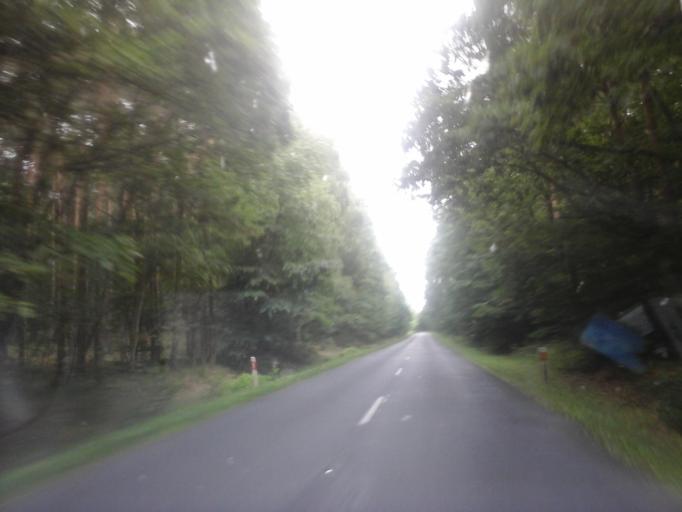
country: PL
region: West Pomeranian Voivodeship
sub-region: Powiat stargardzki
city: Kobylanka
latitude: 53.4198
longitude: 14.9295
